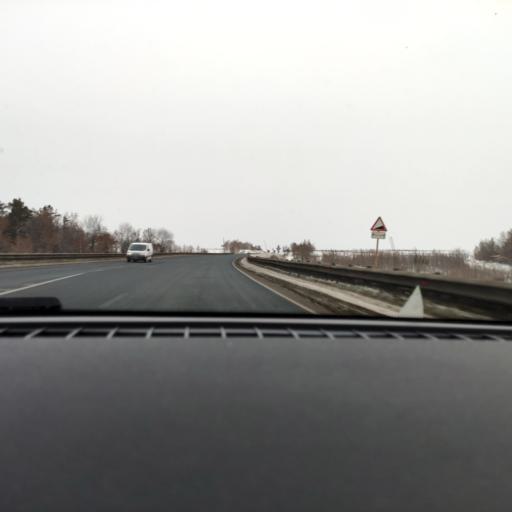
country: RU
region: Samara
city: Novosemeykino
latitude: 53.3601
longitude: 50.4394
